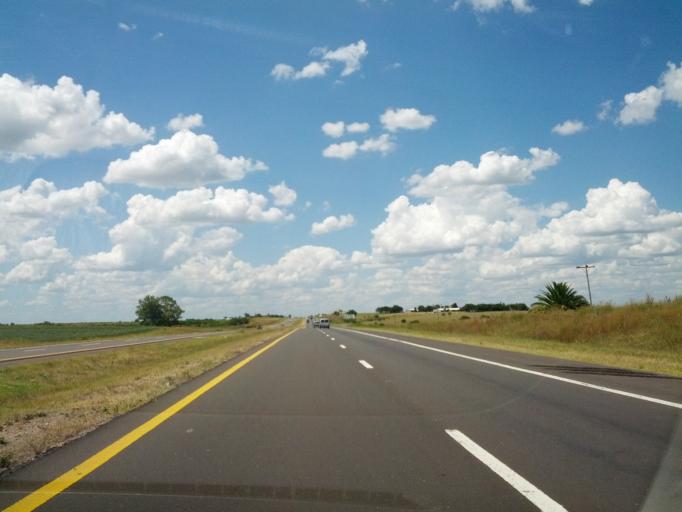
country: AR
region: Entre Rios
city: Colonia Elia
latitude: -32.5661
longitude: -58.3740
